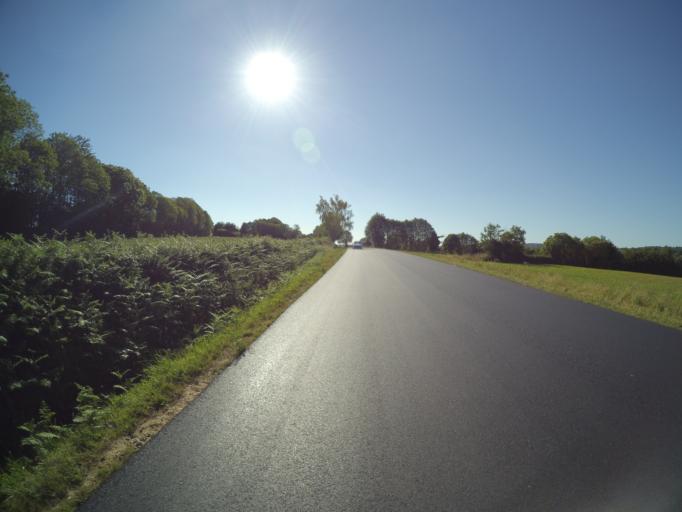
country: FR
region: Pays de la Loire
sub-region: Departement de la Vendee
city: Les Herbiers
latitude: 46.8656
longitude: -0.9781
